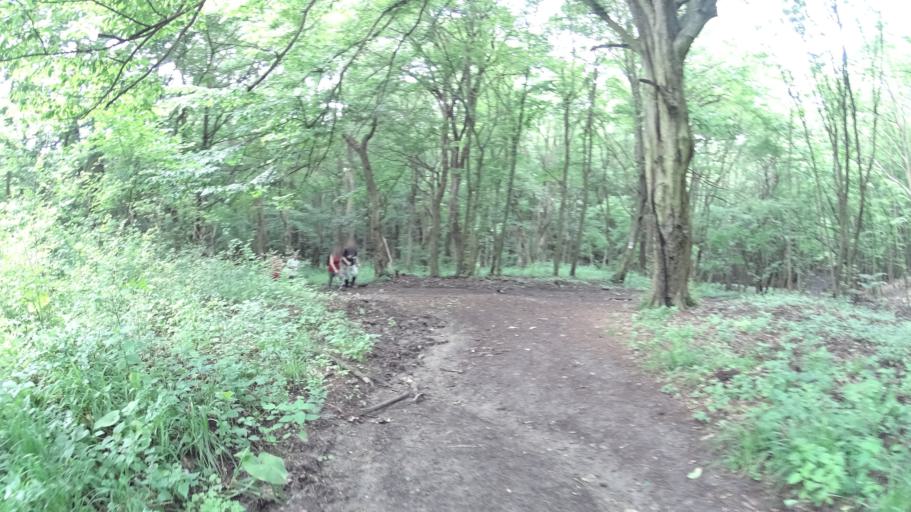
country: HU
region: Pest
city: Nagymaros
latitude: 47.8157
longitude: 18.9350
